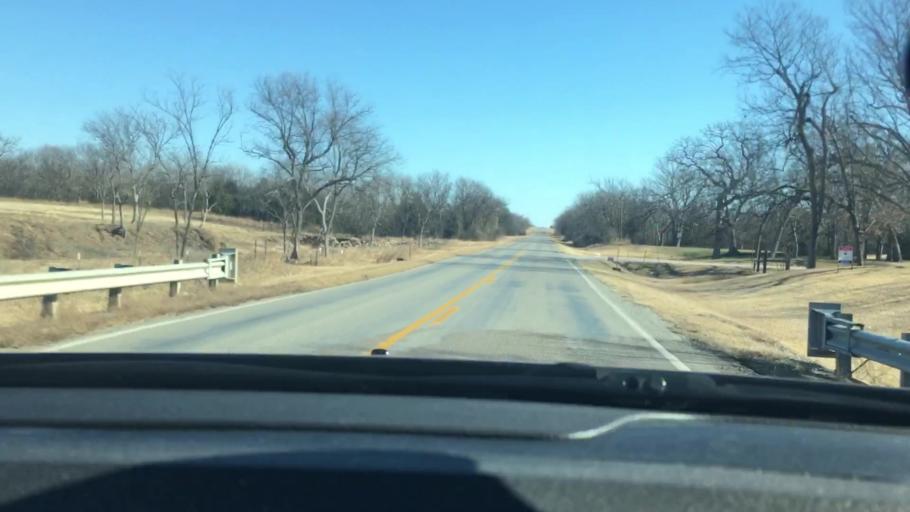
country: US
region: Oklahoma
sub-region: Garvin County
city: Wynnewood
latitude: 34.6515
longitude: -97.1184
